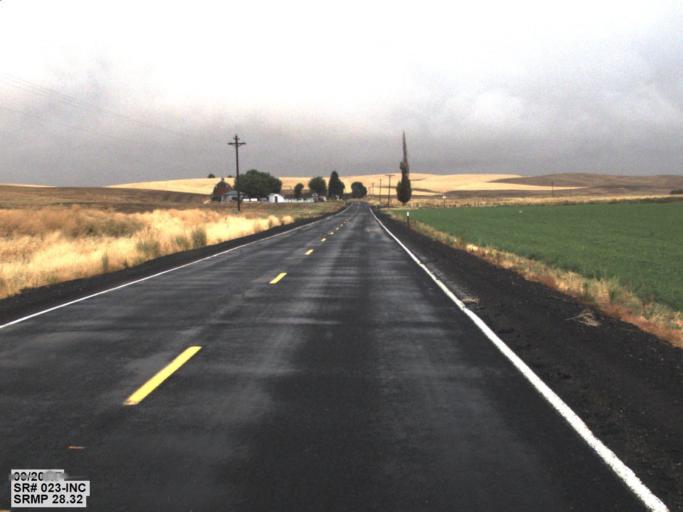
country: US
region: Washington
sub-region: Spokane County
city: Cheney
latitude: 47.1329
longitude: -117.8295
